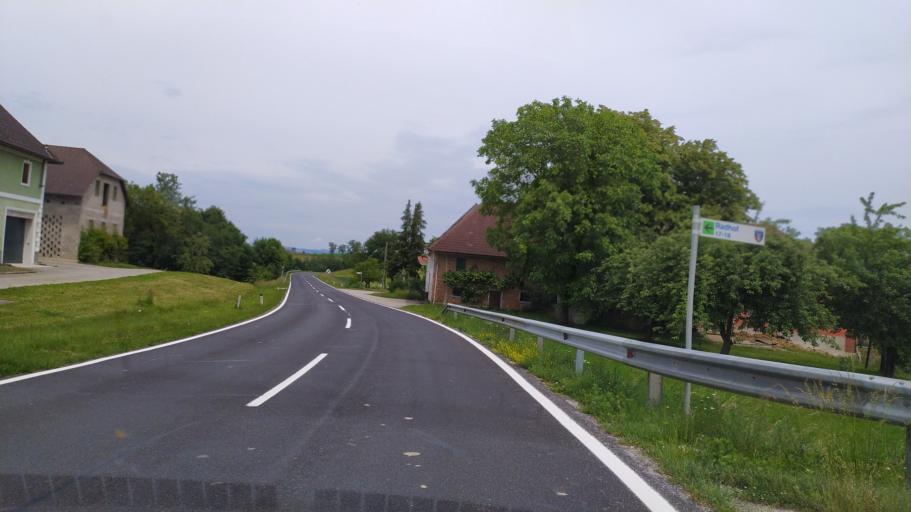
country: AT
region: Lower Austria
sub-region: Politischer Bezirk Amstetten
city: Strengberg
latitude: 48.1340
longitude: 14.6075
